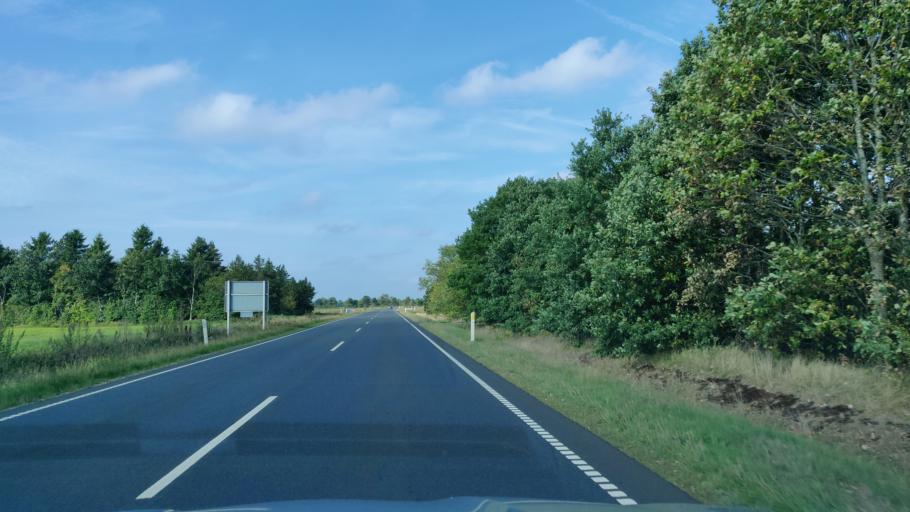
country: DK
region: Central Jutland
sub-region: Herning Kommune
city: Sunds
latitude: 56.2663
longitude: 8.9983
